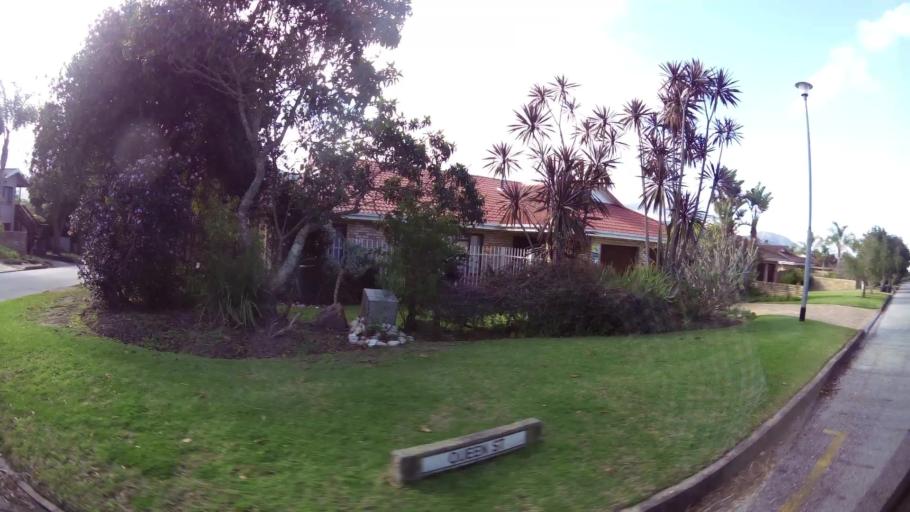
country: ZA
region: Western Cape
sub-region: Eden District Municipality
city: George
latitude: -33.9557
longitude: 22.4742
